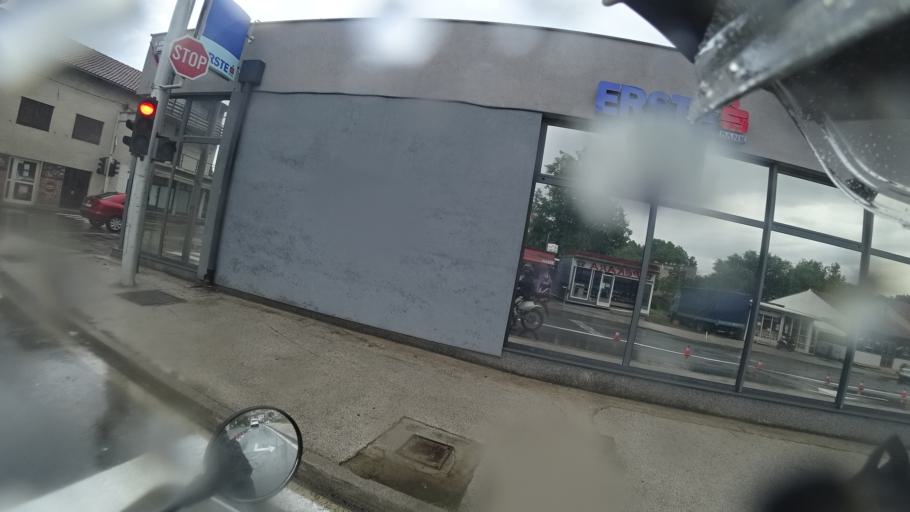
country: HR
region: Sibensko-Kniniska
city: Knin
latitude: 44.0426
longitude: 16.1978
